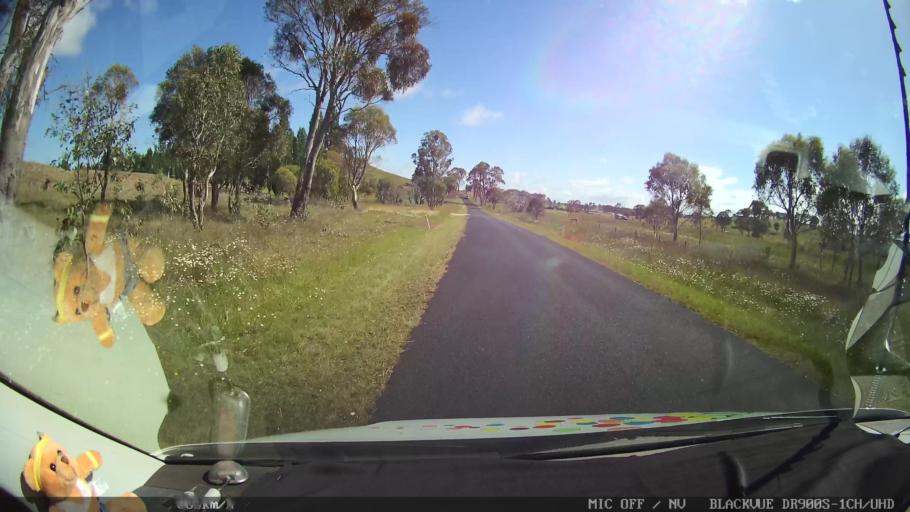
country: AU
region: New South Wales
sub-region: Guyra
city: Guyra
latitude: -30.1765
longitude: 151.6834
